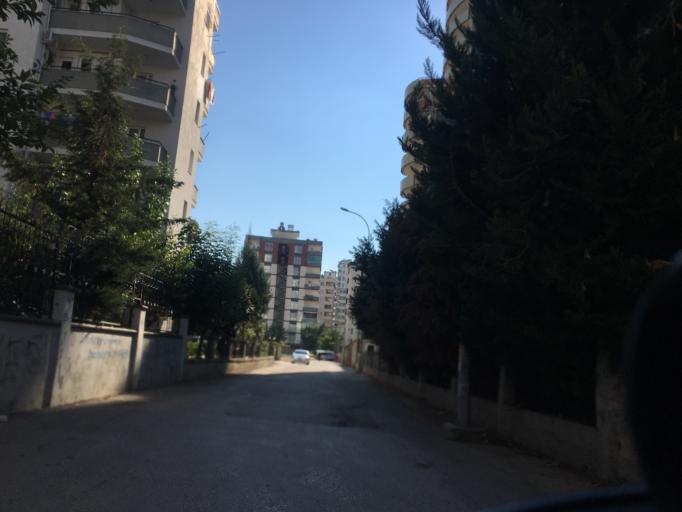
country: TR
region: Adana
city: Seyhan
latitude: 37.0221
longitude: 35.2861
